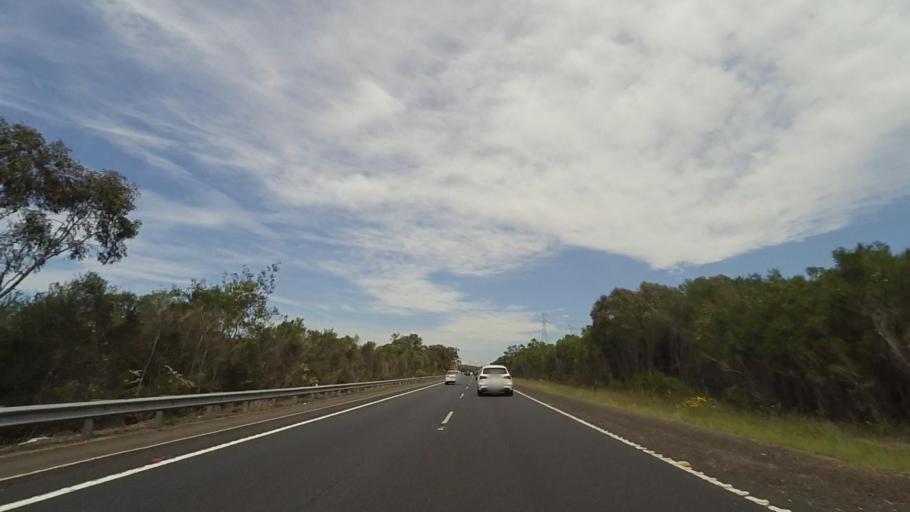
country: AU
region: New South Wales
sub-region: Wollongong
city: Helensburgh
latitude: -34.1856
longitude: 150.9702
